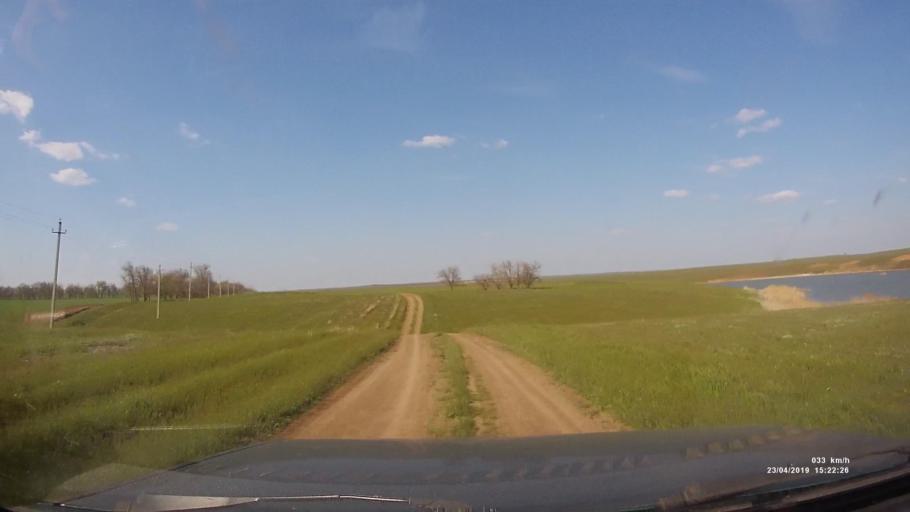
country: RU
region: Rostov
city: Remontnoye
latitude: 46.5290
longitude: 42.9698
